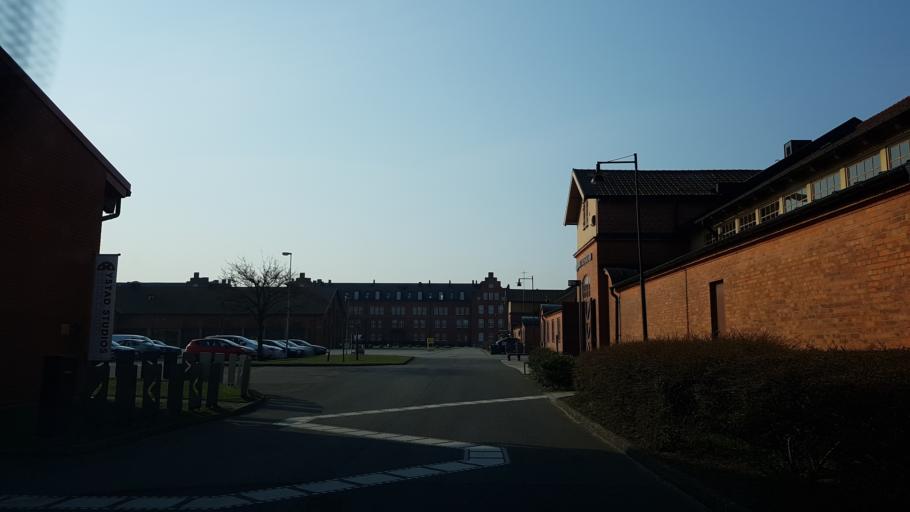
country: SE
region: Skane
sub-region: Ystads Kommun
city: Ystad
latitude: 55.4340
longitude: 13.8437
